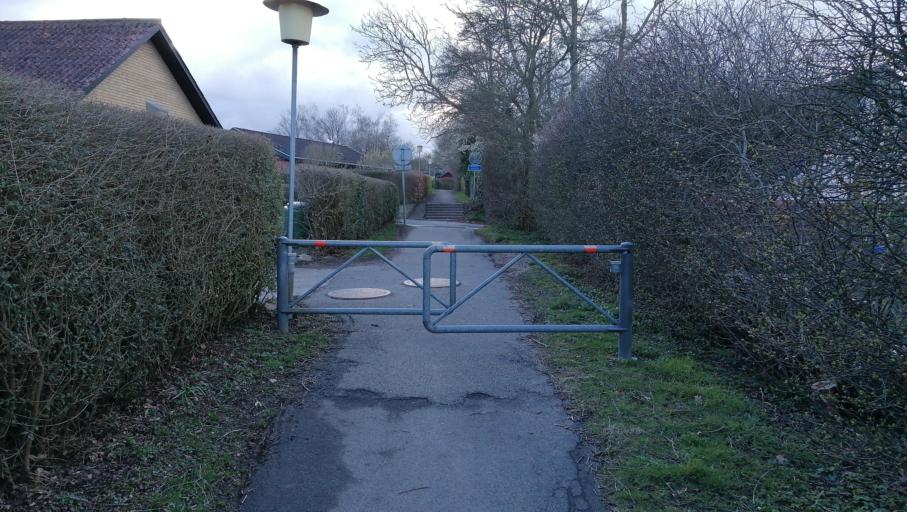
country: DK
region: Zealand
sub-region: Odsherred Kommune
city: Horve
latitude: 55.7489
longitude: 11.4505
